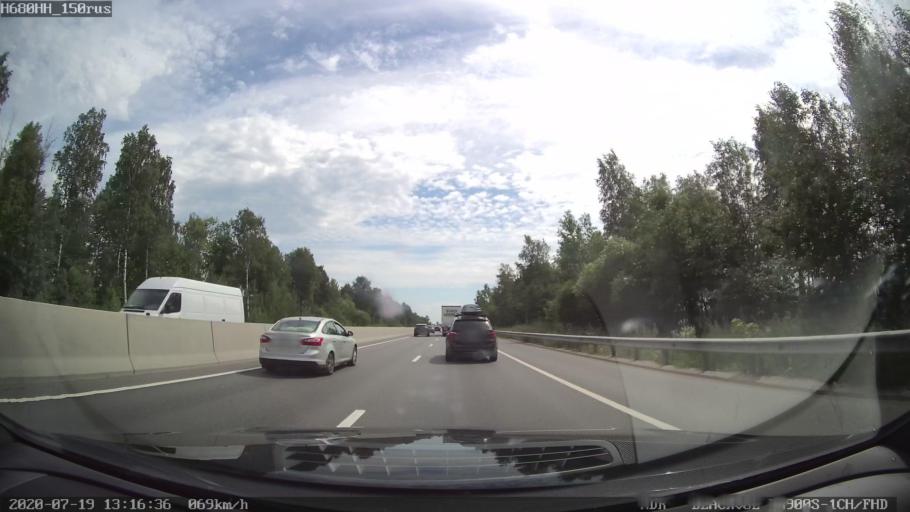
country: RU
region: St.-Petersburg
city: Kolpino
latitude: 59.7158
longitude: 30.5572
